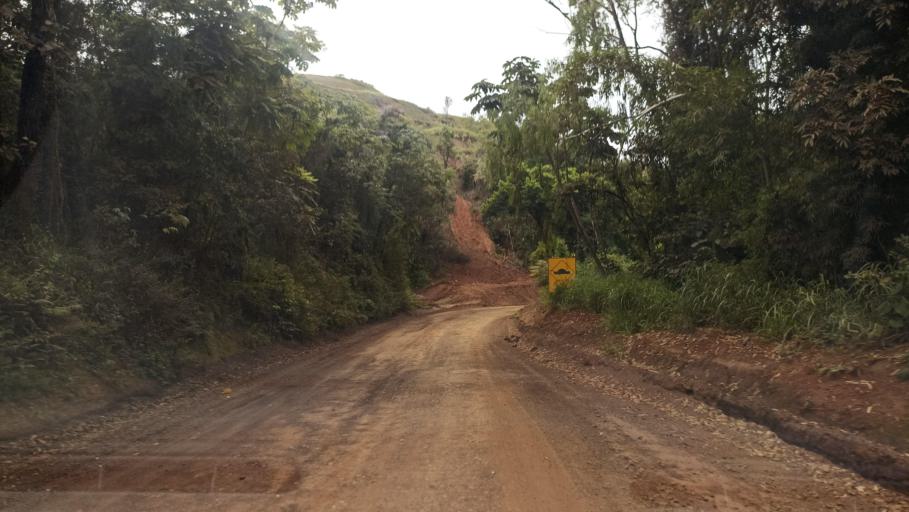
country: BR
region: Minas Gerais
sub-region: Congonhas
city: Congonhas
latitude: -20.4329
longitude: -43.7701
